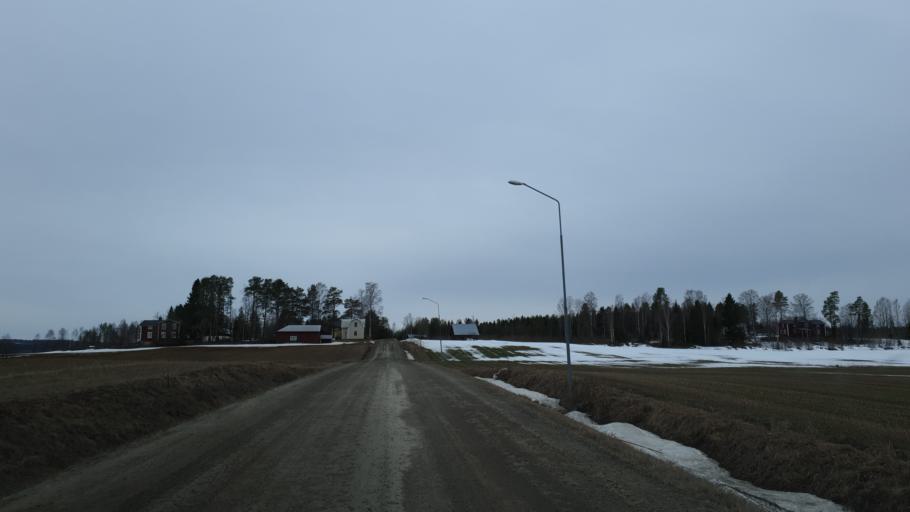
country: SE
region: Vaesterbotten
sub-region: Robertsfors Kommun
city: Robertsfors
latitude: 64.3786
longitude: 20.9091
